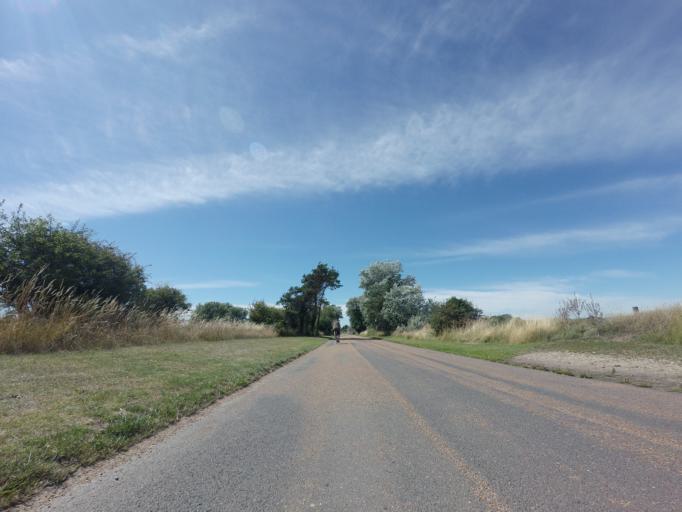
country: GB
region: England
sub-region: Kent
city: Sandwich
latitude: 51.2695
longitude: 1.3713
